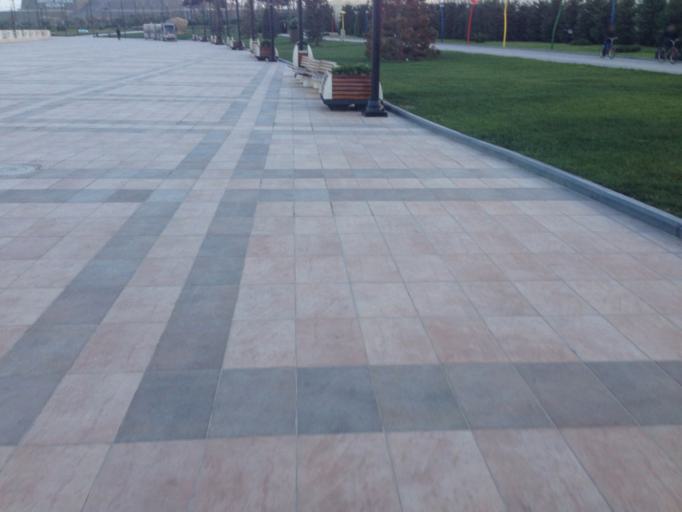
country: AZ
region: Baki
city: Badamdar
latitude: 40.3478
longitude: 49.8394
